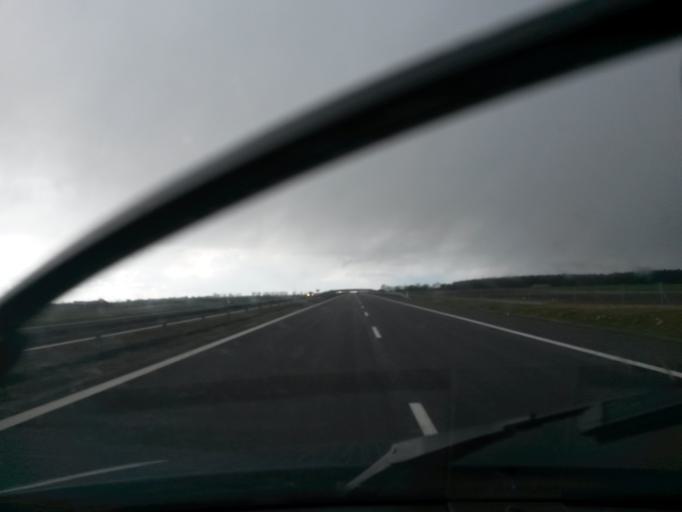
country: PL
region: Greater Poland Voivodeship
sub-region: Powiat sredzki
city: Sroda Wielkopolska
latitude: 52.3102
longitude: 17.2593
